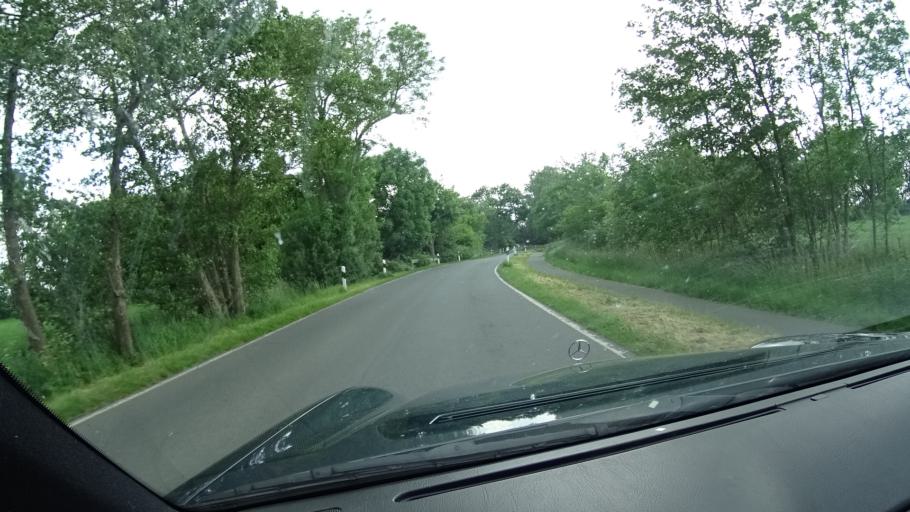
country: DE
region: Lower Saxony
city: Butjadingen
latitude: 53.5772
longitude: 8.2664
